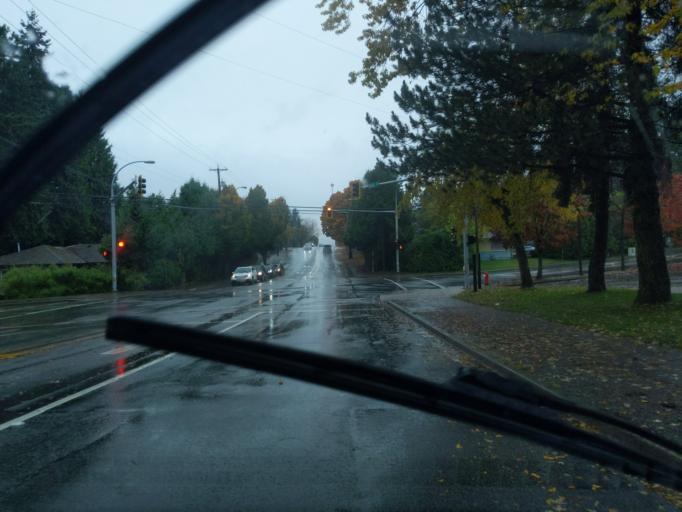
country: CA
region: British Columbia
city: New Westminster
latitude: 49.1917
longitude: -122.8629
